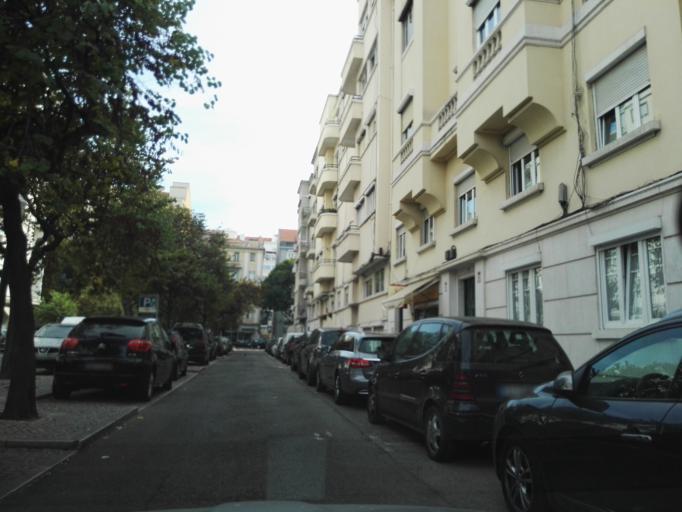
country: PT
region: Lisbon
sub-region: Lisbon
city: Lisbon
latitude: 38.7393
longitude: -9.1515
